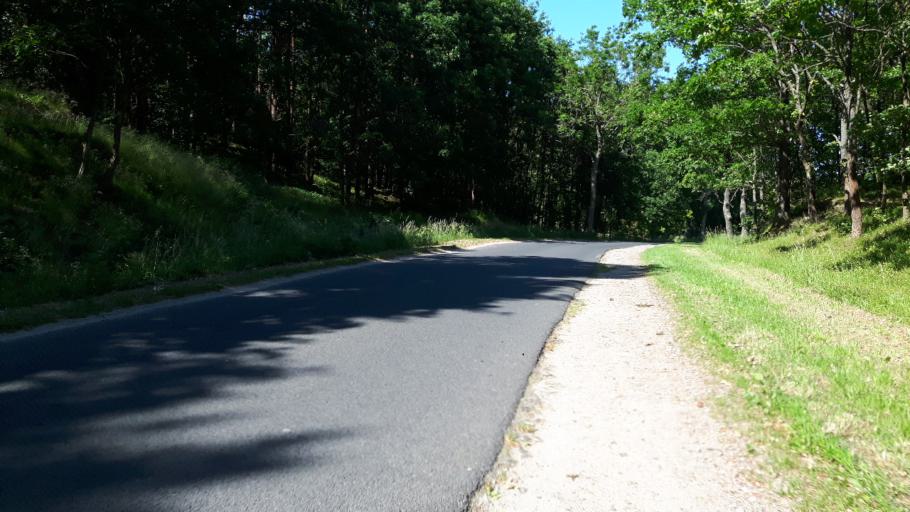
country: PL
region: Pomeranian Voivodeship
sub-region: Powiat slupski
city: Glowczyce
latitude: 54.6693
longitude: 17.4194
